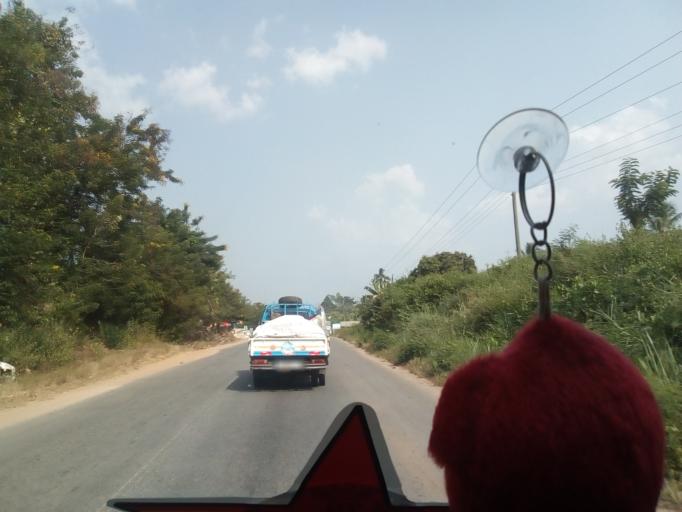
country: GH
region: Eastern
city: Suhum
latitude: 6.0439
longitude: -0.4256
